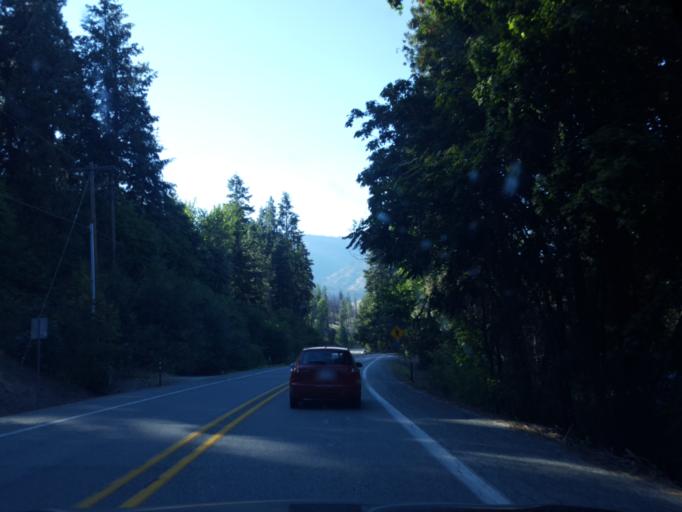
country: US
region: Washington
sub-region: Chelan County
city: Granite Falls
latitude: 47.8719
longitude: -120.1982
